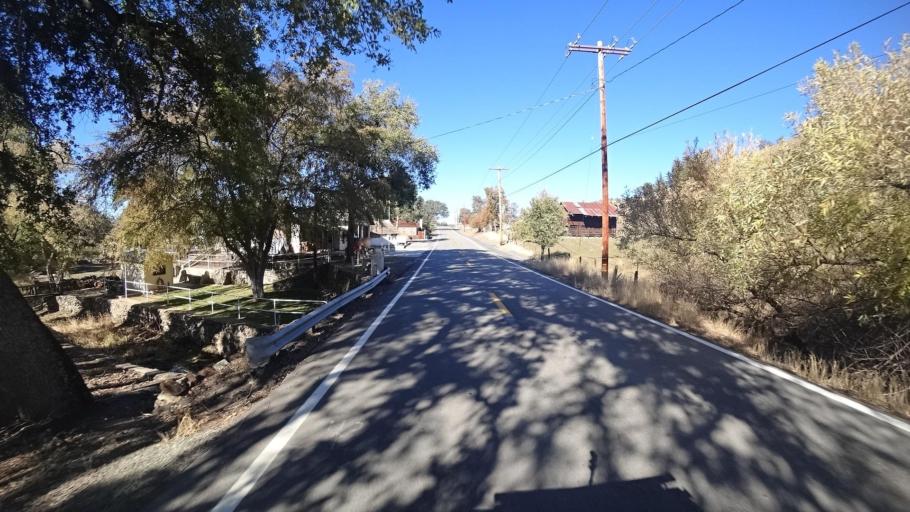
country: US
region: California
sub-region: Kern County
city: Alta Sierra
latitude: 35.7264
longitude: -118.7003
